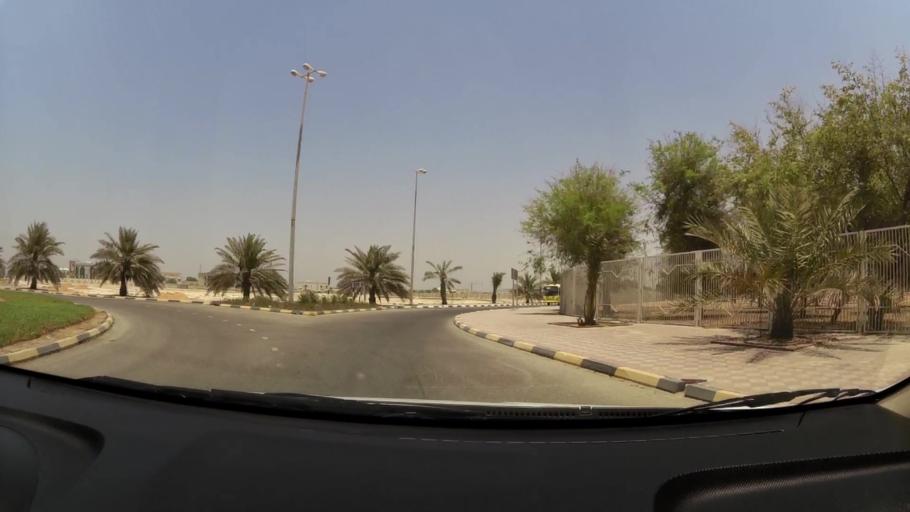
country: AE
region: Umm al Qaywayn
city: Umm al Qaywayn
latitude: 25.5310
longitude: 55.5312
